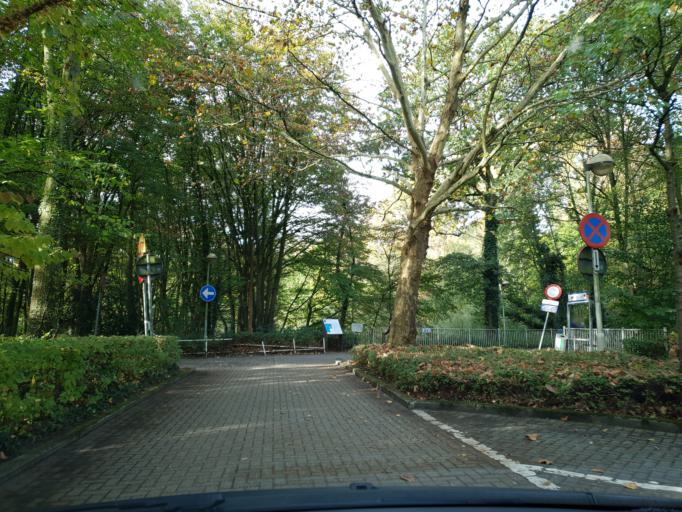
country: BE
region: Flanders
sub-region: Provincie Antwerpen
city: Schoten
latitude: 51.2610
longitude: 4.4592
